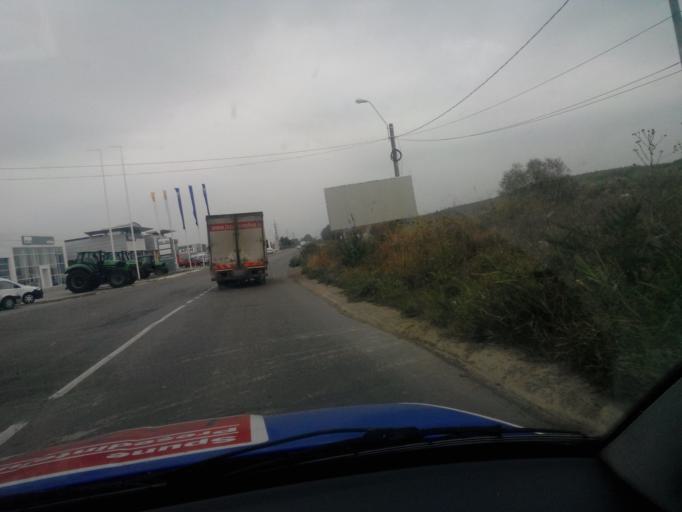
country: RO
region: Braila
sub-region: Municipiul Braila
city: Braila
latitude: 45.3007
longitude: 27.9819
